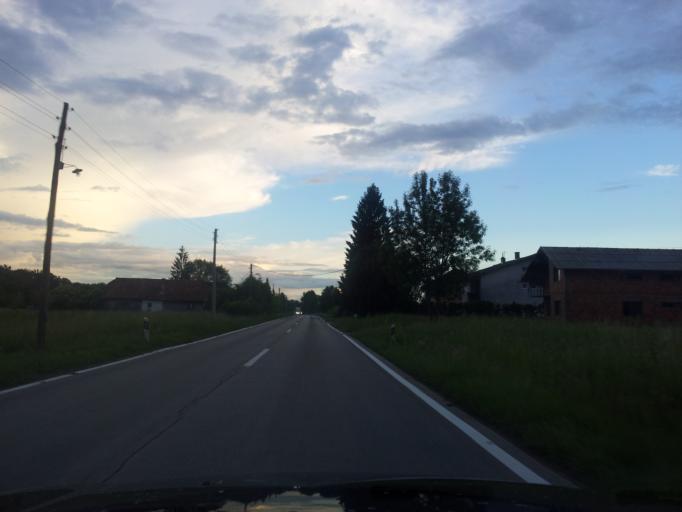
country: HR
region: Karlovacka
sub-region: Grad Karlovac
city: Karlovac
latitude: 45.5580
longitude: 15.5777
